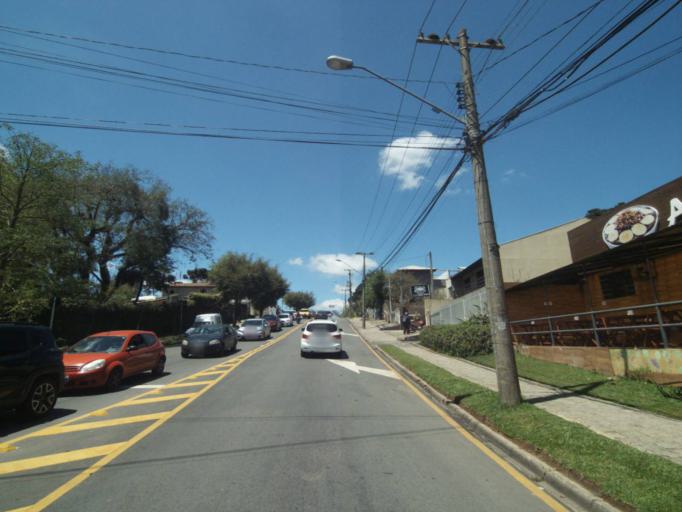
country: BR
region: Parana
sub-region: Curitiba
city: Curitiba
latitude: -25.3882
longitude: -49.2665
